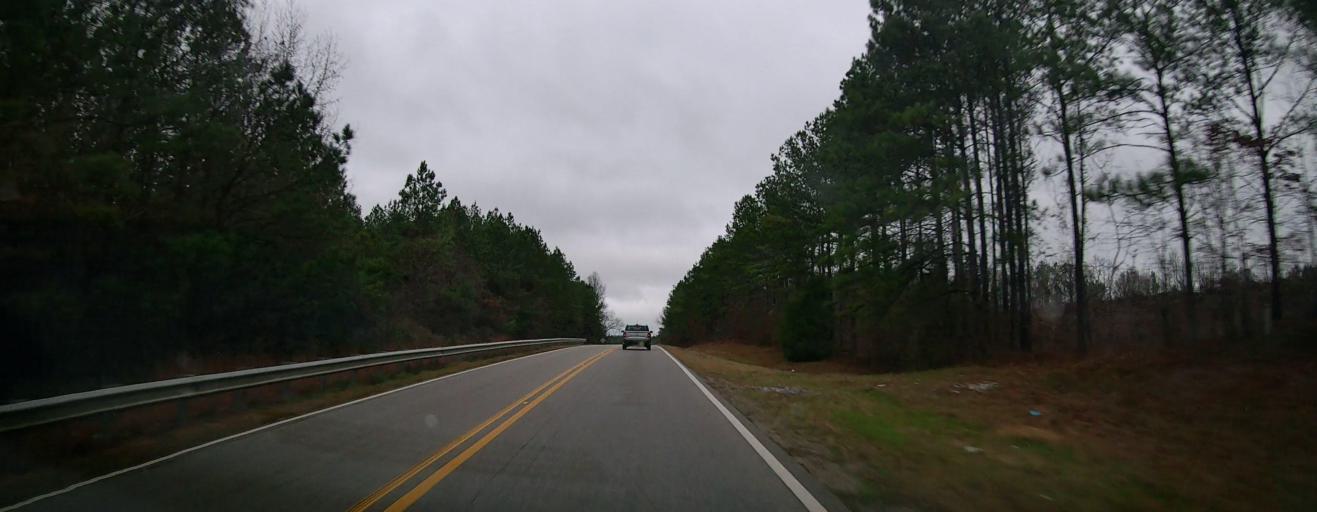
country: US
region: Alabama
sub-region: Bibb County
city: Centreville
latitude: 32.8645
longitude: -86.9702
